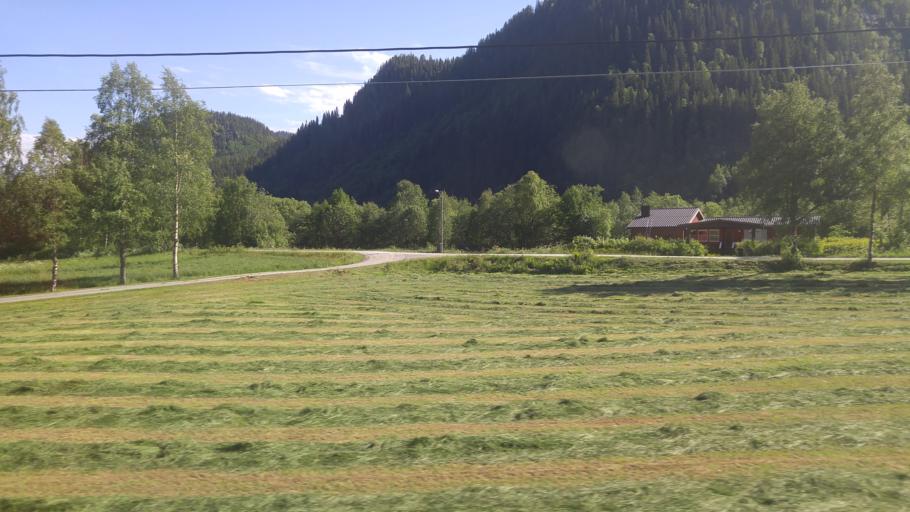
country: NO
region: Sor-Trondelag
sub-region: Midtre Gauldal
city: Storen
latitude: 63.0200
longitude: 10.4305
